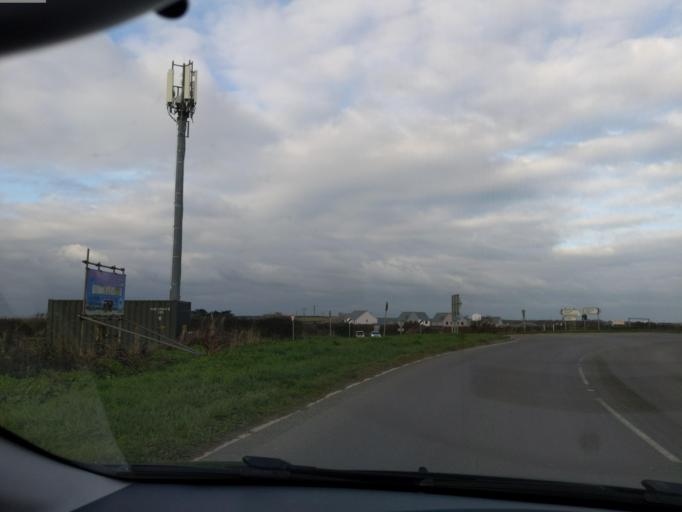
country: GB
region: England
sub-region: Cornwall
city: Padstow
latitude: 50.5331
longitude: -4.9510
